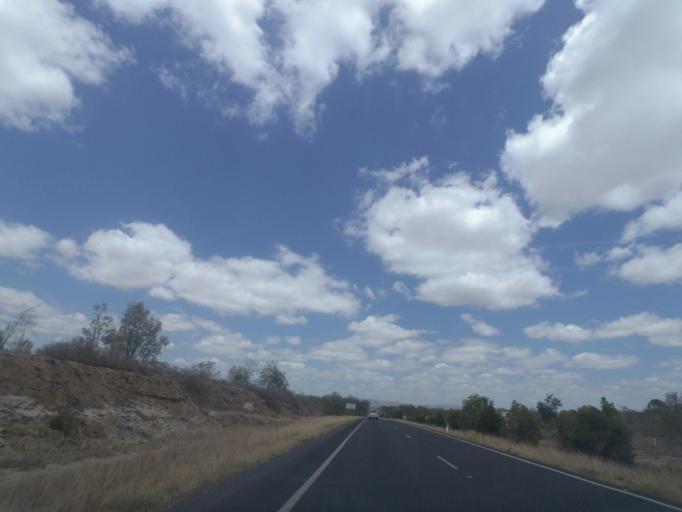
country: AU
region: Queensland
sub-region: Lockyer Valley
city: Gatton
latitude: -27.5521
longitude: 152.1553
